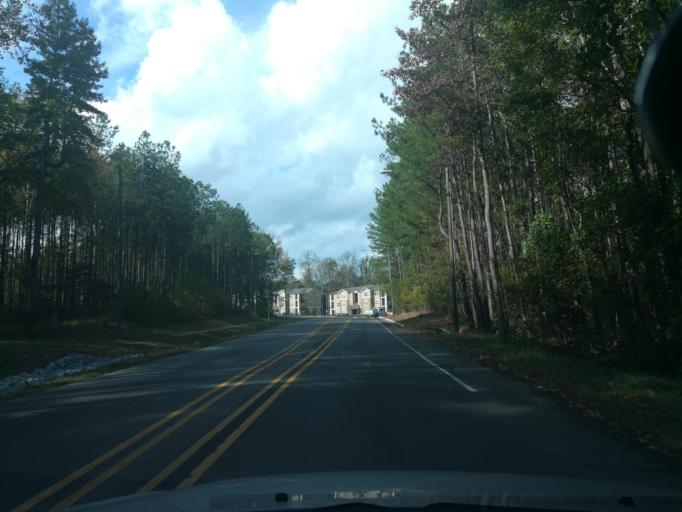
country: US
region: North Carolina
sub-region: Durham County
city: Durham
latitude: 36.0561
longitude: -78.9361
